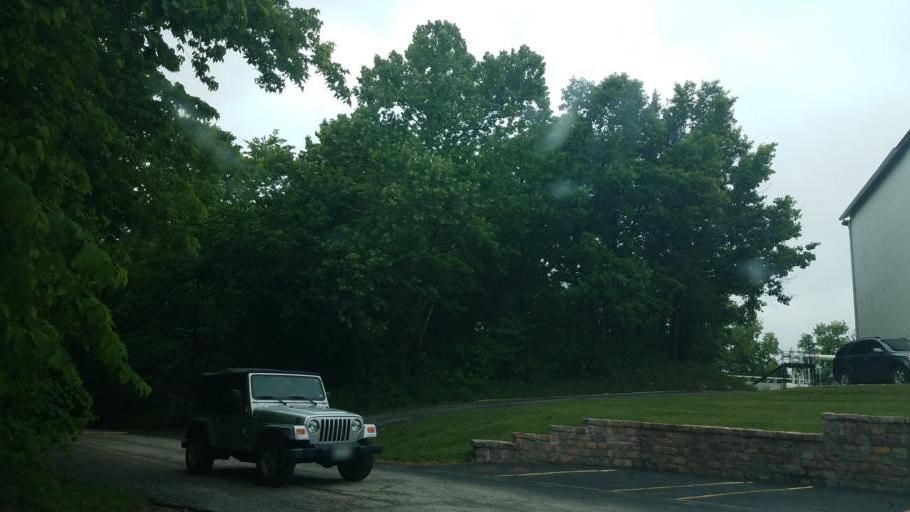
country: US
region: Missouri
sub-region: Moniteau County
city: California
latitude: 38.5901
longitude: -92.5697
